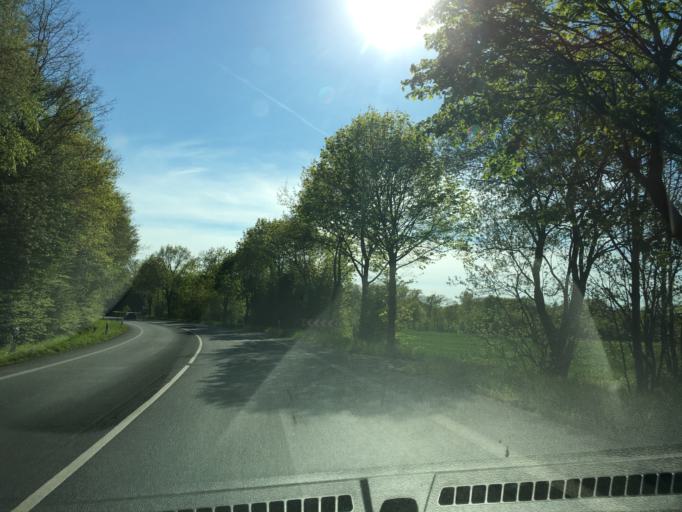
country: DE
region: North Rhine-Westphalia
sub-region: Regierungsbezirk Munster
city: Senden
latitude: 51.9222
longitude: 7.5061
